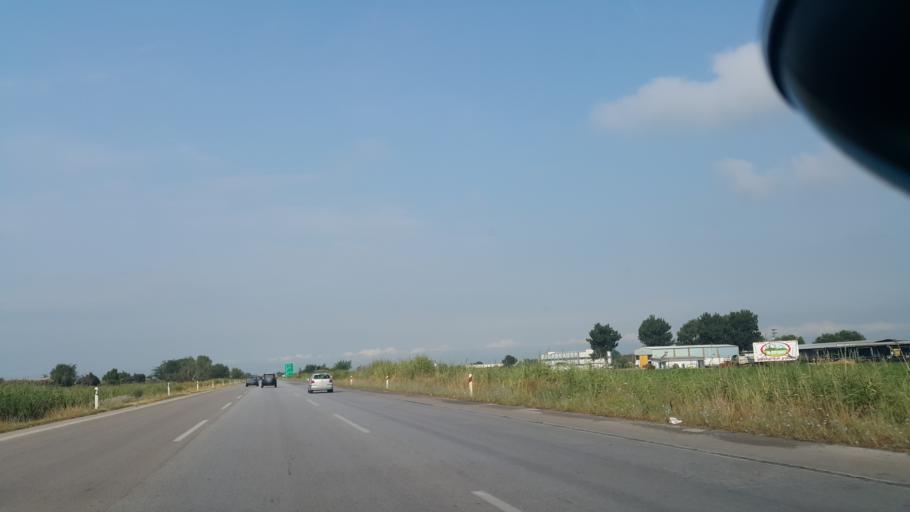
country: GR
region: Central Macedonia
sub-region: Nomos Thessalonikis
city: Chalastra
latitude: 40.6214
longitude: 22.7569
